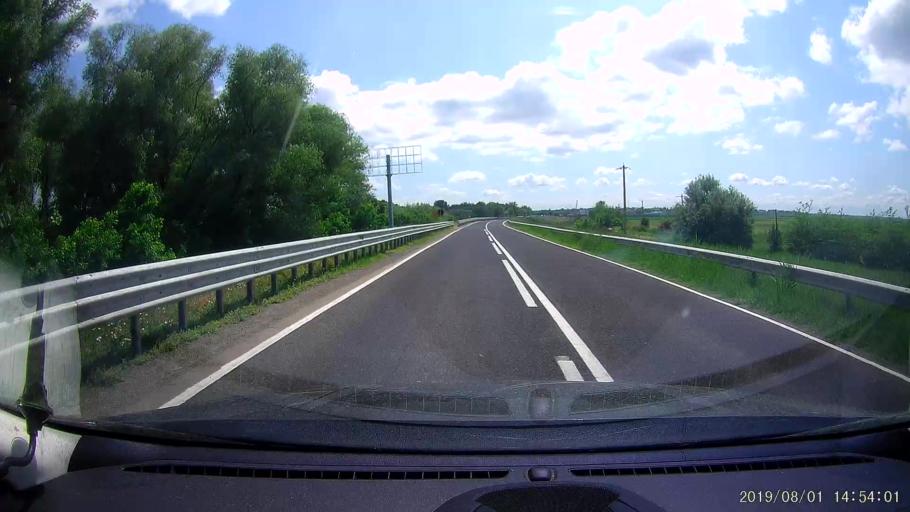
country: RO
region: Braila
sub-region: Municipiul Braila
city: Braila
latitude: 45.3245
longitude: 27.9956
